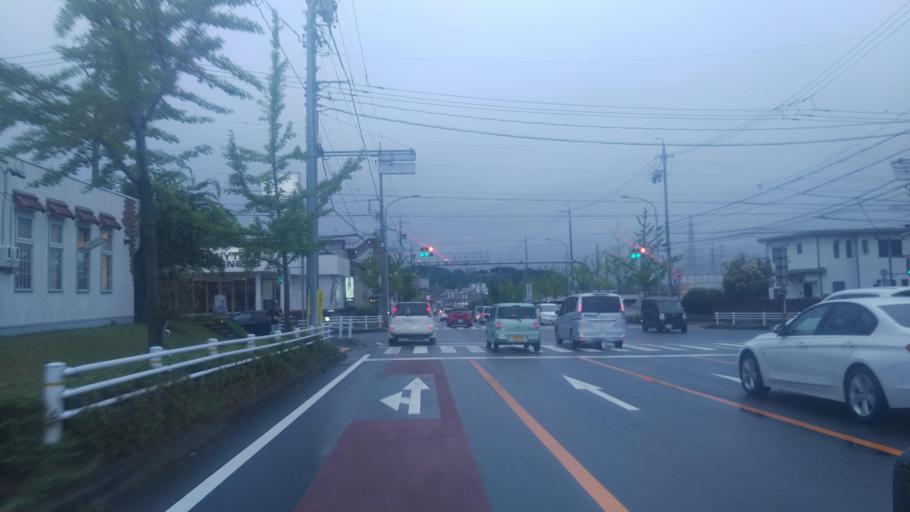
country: JP
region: Aichi
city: Kasugai
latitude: 35.2346
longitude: 137.0006
